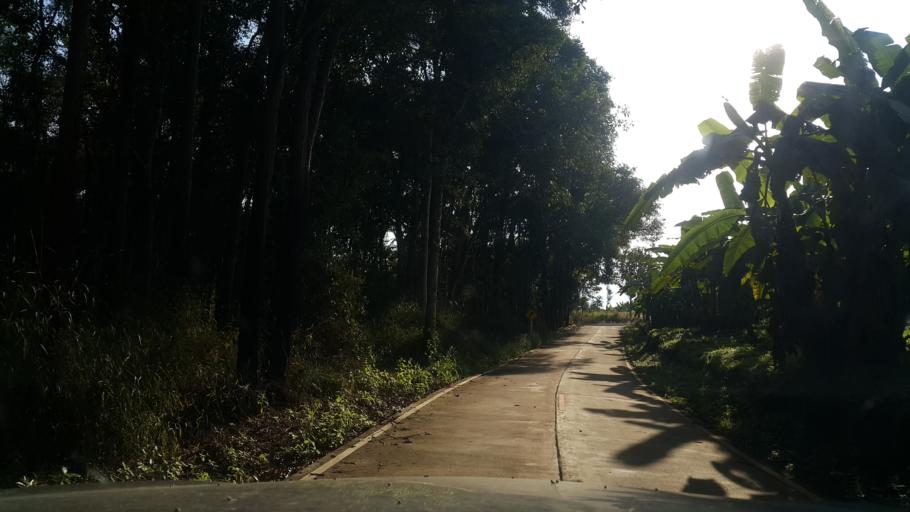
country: TH
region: Chiang Mai
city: Samoeng
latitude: 19.0009
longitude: 98.6844
